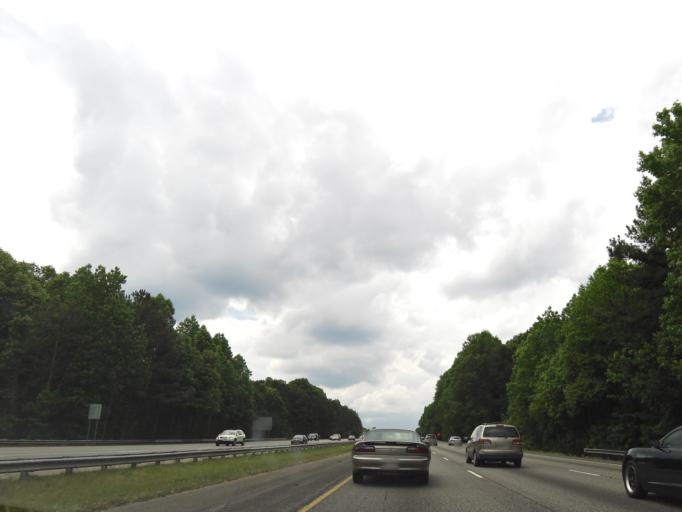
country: US
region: Georgia
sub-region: Cobb County
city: Austell
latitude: 33.7749
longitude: -84.6226
